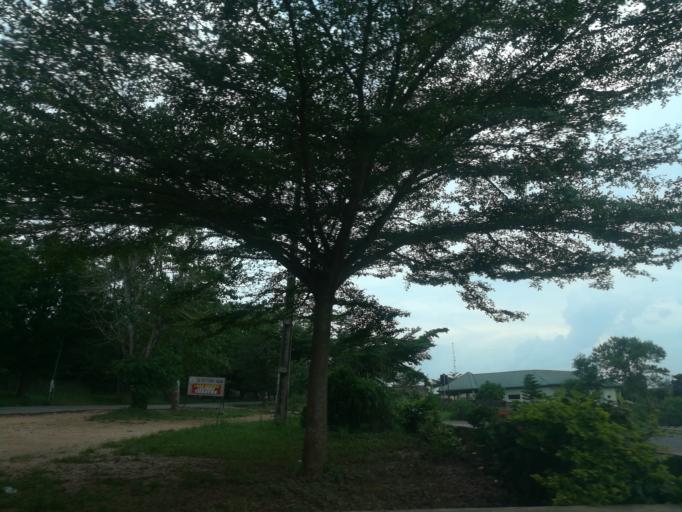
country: NG
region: Oyo
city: Ibadan
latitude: 7.4342
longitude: 3.8879
